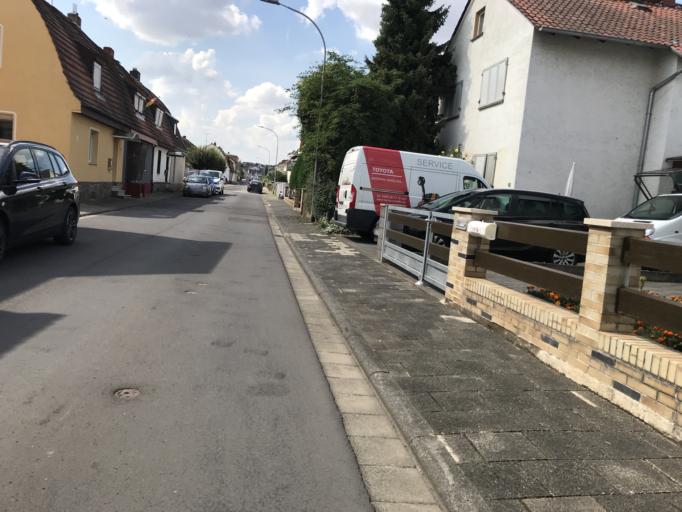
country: DE
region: Hesse
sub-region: Regierungsbezirk Darmstadt
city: Wolfersheim
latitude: 50.3975
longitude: 8.8224
